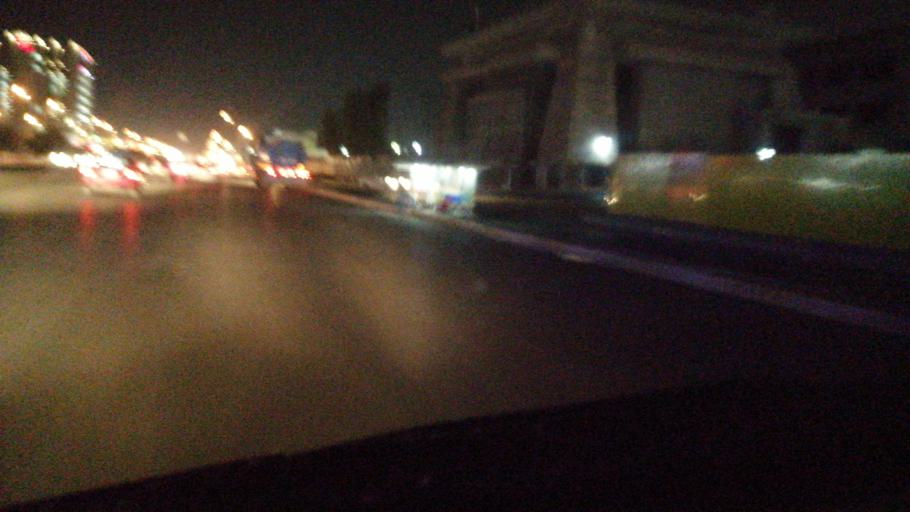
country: IQ
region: Arbil
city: Erbil
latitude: 36.1574
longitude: 43.9862
